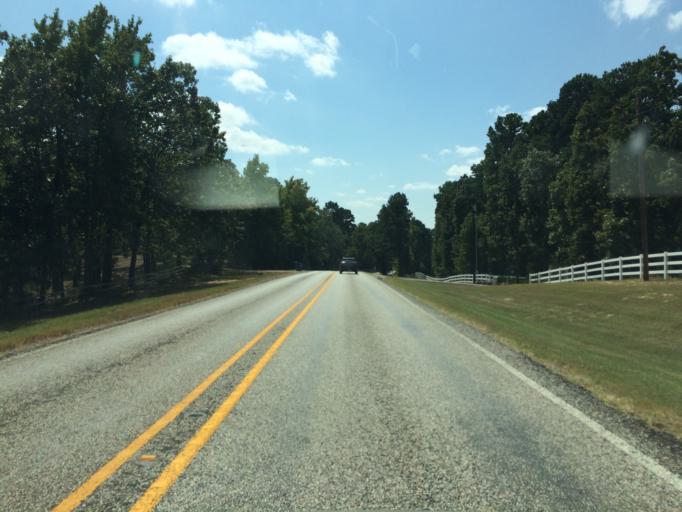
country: US
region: Texas
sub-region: Wood County
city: Hawkins
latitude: 32.6441
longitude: -95.2489
